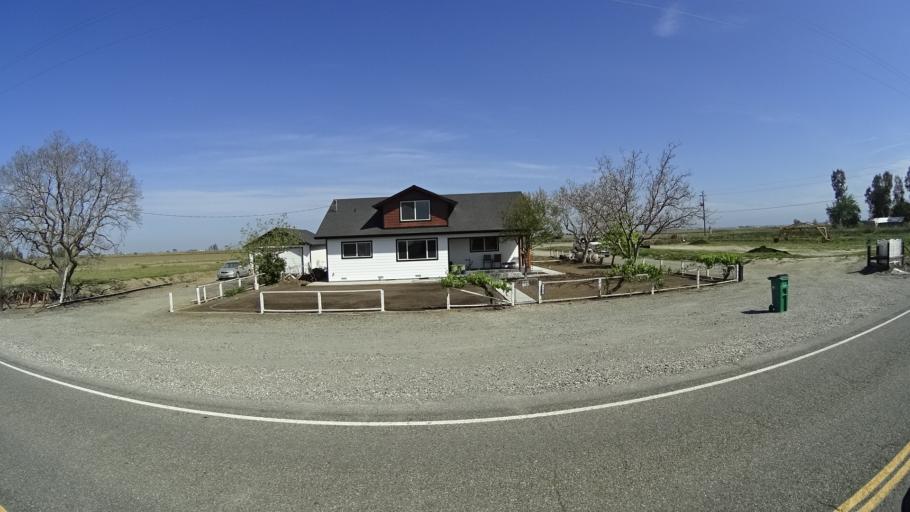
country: US
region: California
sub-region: Glenn County
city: Willows
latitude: 39.5826
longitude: -122.0566
